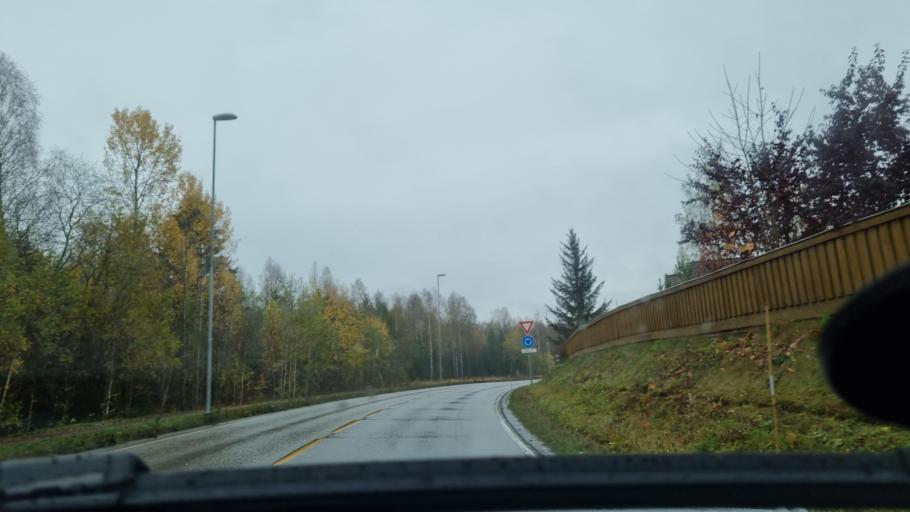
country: NO
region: Hedmark
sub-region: Hamar
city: Hamar
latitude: 60.8168
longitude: 11.0648
